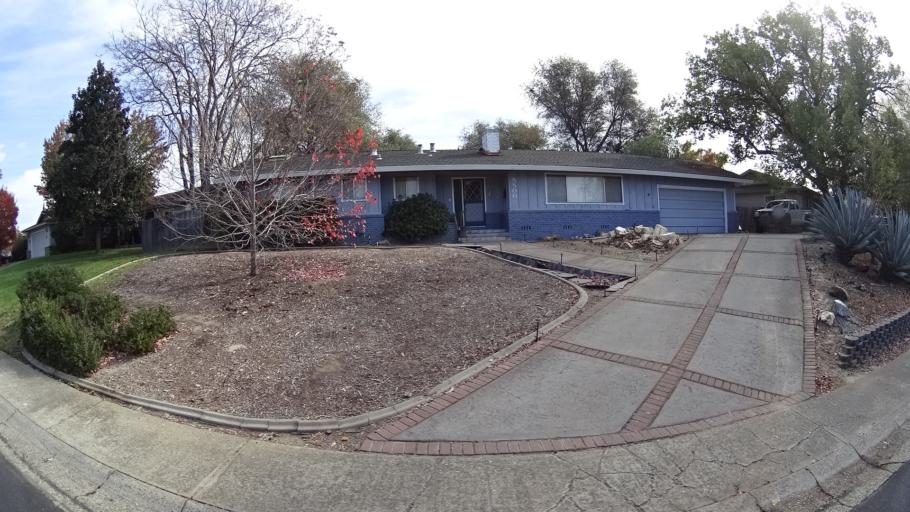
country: US
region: California
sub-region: Sacramento County
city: Fair Oaks
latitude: 38.6669
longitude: -121.2787
